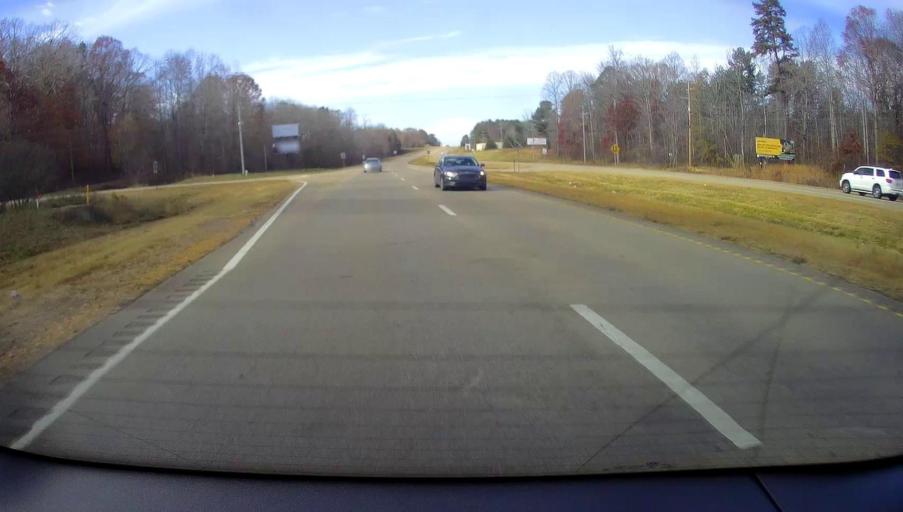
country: US
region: Mississippi
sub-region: Alcorn County
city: Farmington
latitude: 34.8912
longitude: -88.4628
